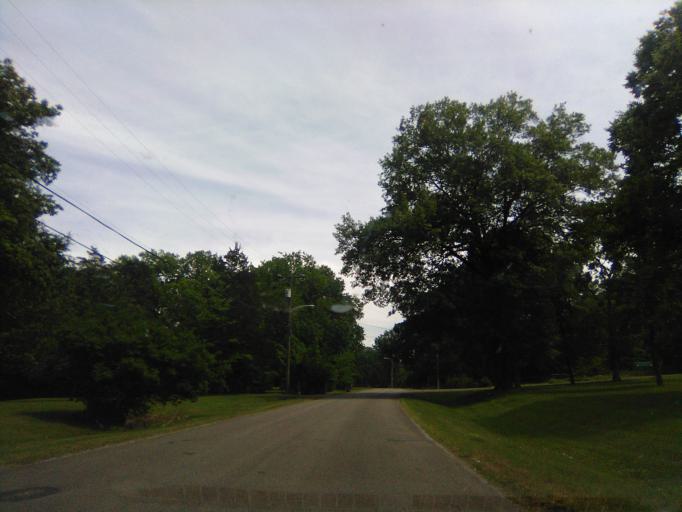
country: US
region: Tennessee
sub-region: Davidson County
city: Belle Meade
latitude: 36.1213
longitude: -86.8929
